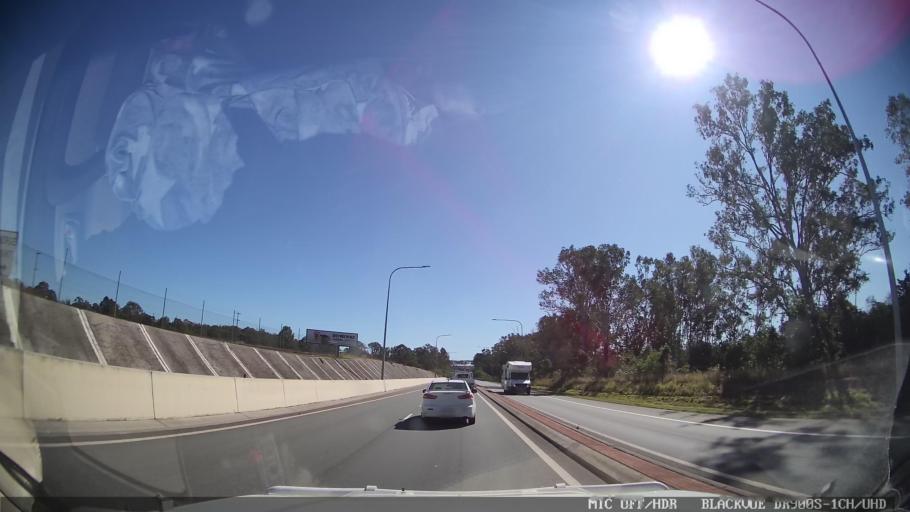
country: AU
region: Queensland
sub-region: Gympie Regional Council
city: Monkland
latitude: -26.2360
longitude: 152.6989
